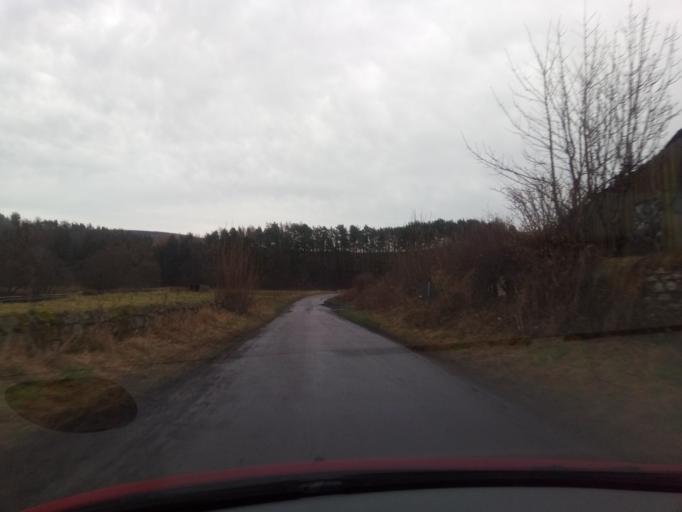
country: GB
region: England
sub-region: Northumberland
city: Wooler
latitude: 55.4951
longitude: -1.9105
